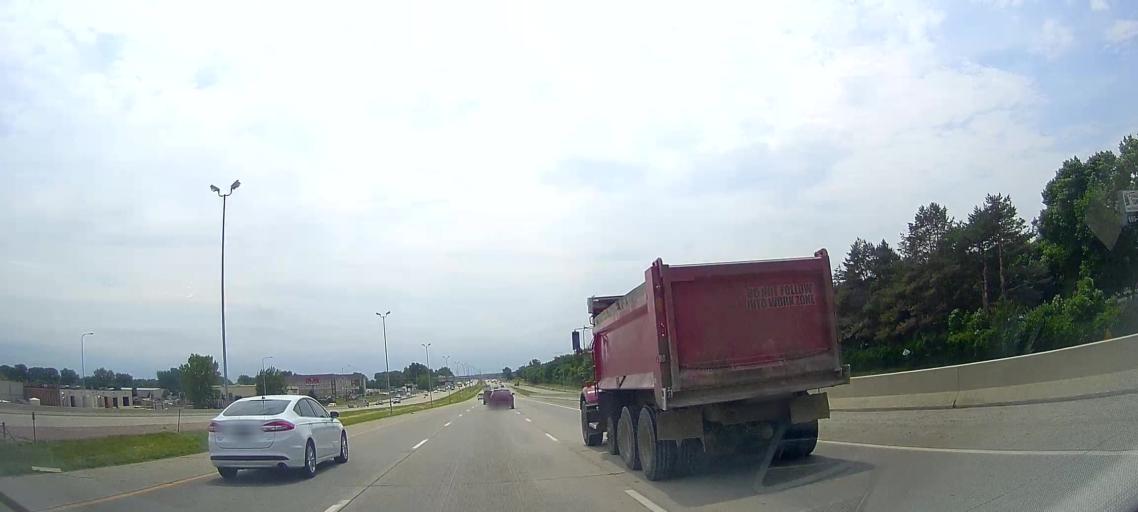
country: US
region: South Dakota
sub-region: Minnehaha County
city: Sioux Falls
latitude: 43.5426
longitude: -96.7804
